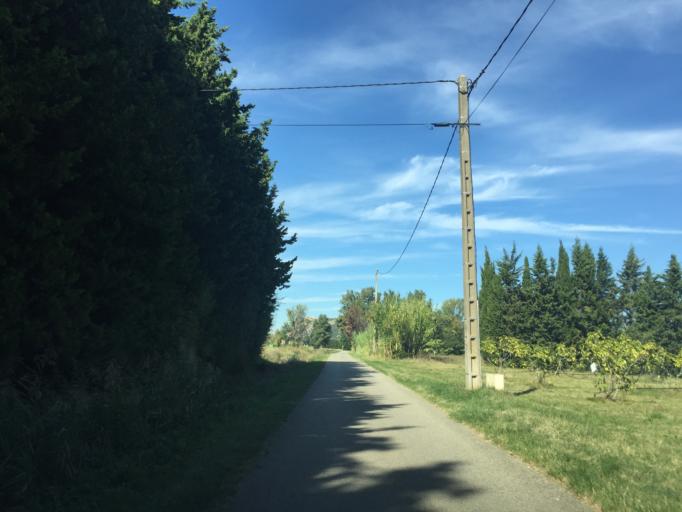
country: FR
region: Provence-Alpes-Cote d'Azur
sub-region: Departement du Vaucluse
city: Mornas
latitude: 44.1837
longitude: 4.7342
